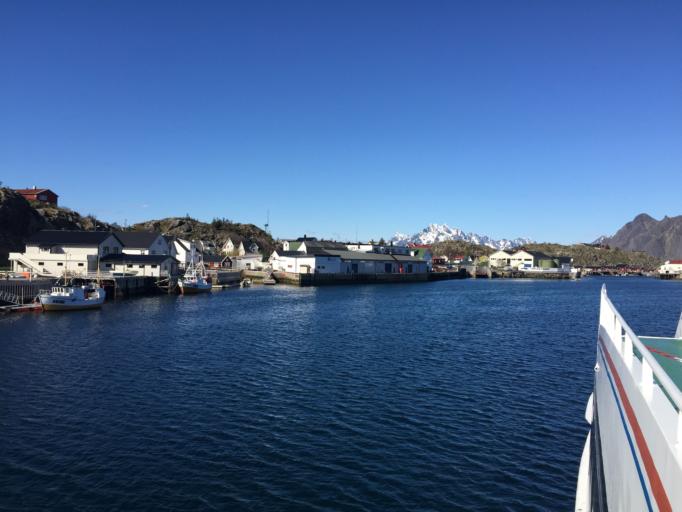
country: NO
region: Nordland
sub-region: Vagan
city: Svolvaer
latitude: 68.1646
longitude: 14.6602
